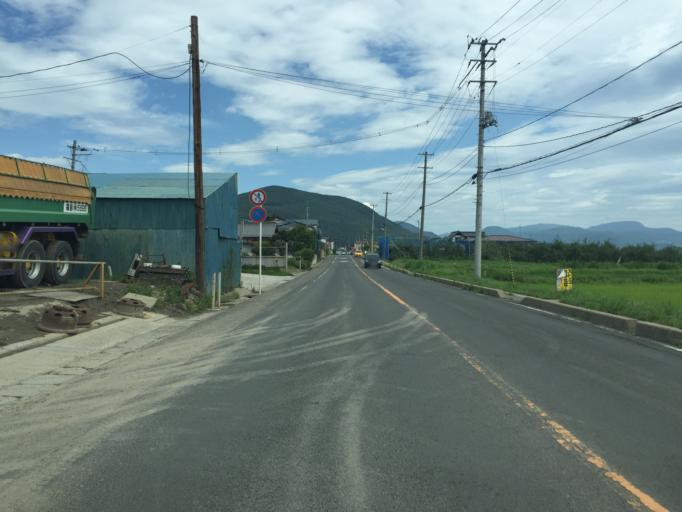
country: JP
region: Fukushima
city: Fukushima-shi
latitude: 37.7902
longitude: 140.3999
